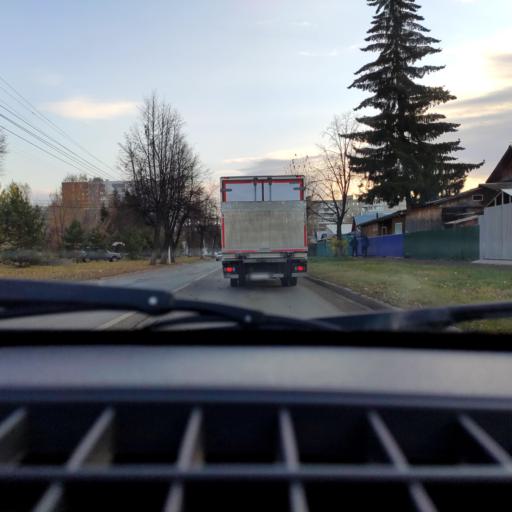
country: RU
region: Bashkortostan
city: Avdon
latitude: 54.7089
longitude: 55.8240
